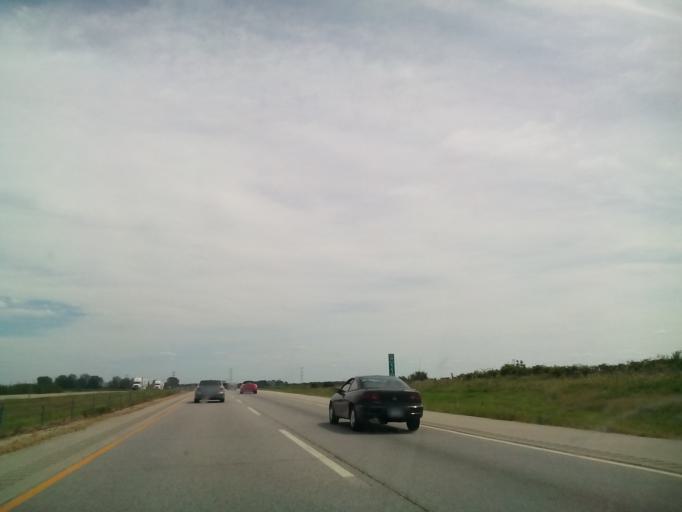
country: US
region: Illinois
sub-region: Kane County
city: Sugar Grove
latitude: 41.8134
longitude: -88.4506
